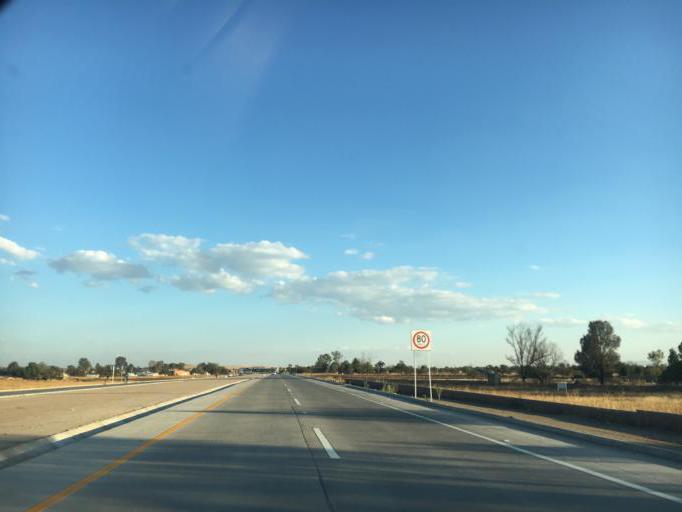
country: MX
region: Guanajuato
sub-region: Leon
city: Ladrilleras del Refugio
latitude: 21.0894
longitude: -101.5599
